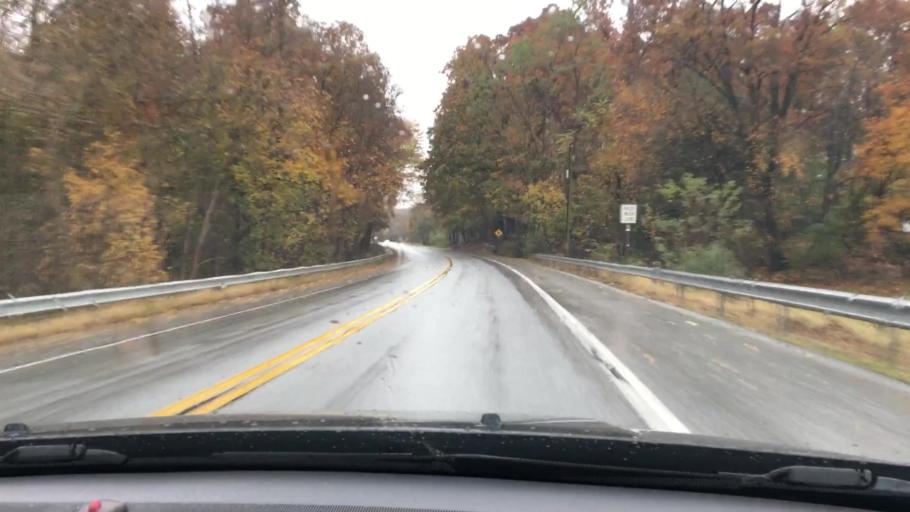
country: US
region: Pennsylvania
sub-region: York County
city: Susquehanna Trails
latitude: 39.8342
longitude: -76.3097
